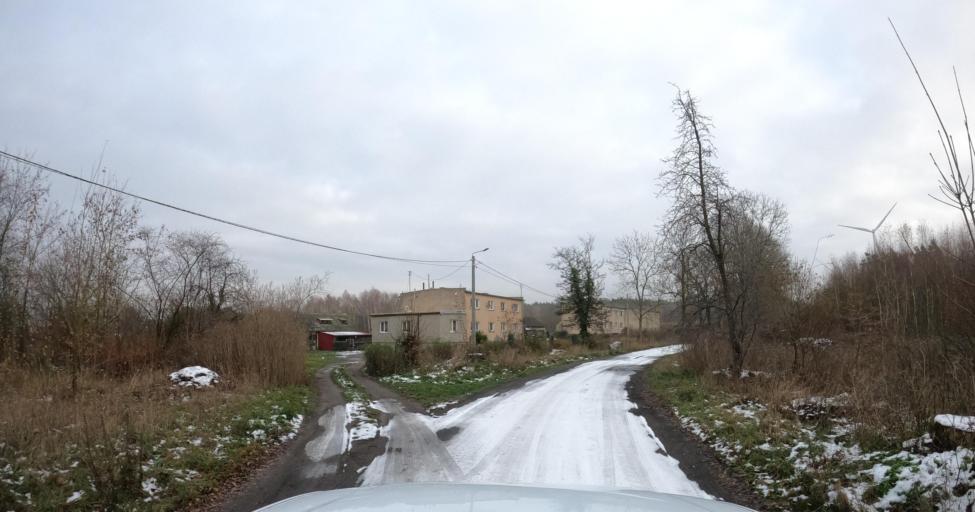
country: PL
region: West Pomeranian Voivodeship
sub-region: Powiat bialogardzki
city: Karlino
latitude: 53.9289
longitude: 15.8304
